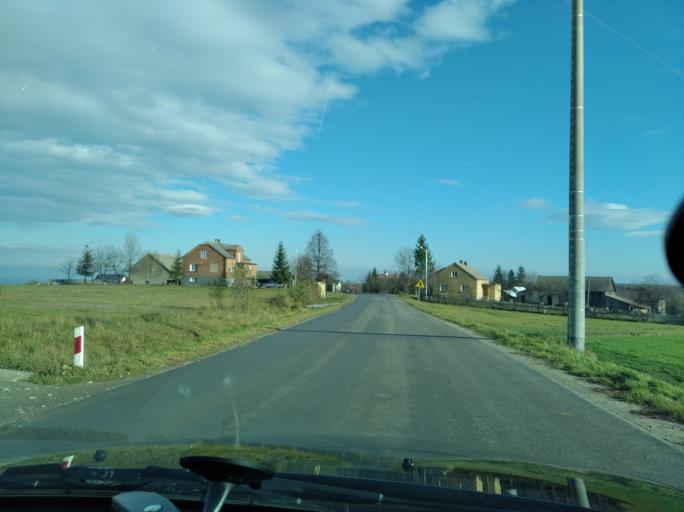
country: PL
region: Subcarpathian Voivodeship
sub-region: Powiat ropczycko-sedziszowski
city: Niedzwiada
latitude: 50.0108
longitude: 21.4798
